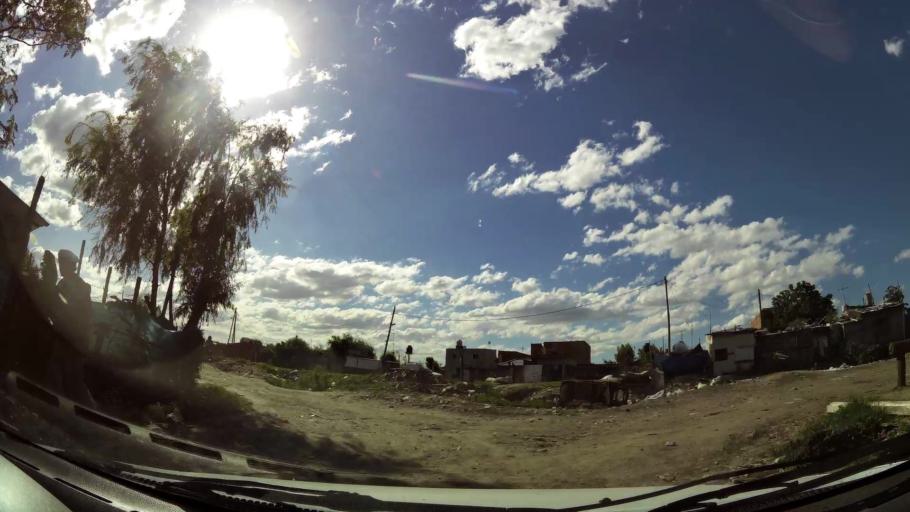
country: AR
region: Buenos Aires
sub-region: Partido de General San Martin
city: General San Martin
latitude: -34.5195
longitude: -58.5836
